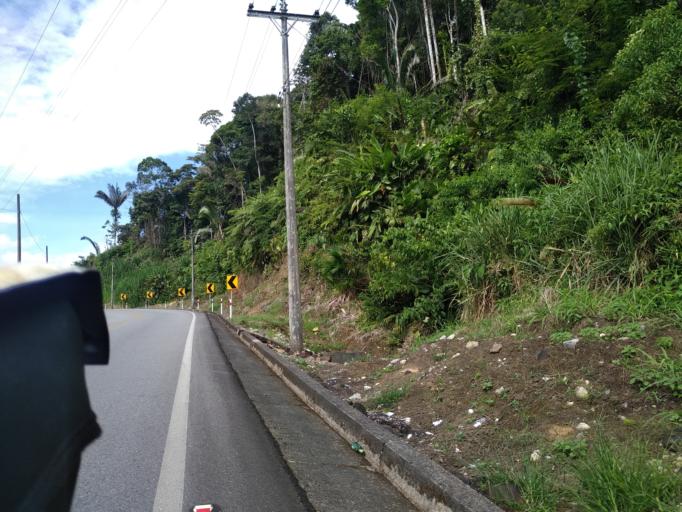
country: EC
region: Napo
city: Tena
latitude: -1.0937
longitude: -77.7935
